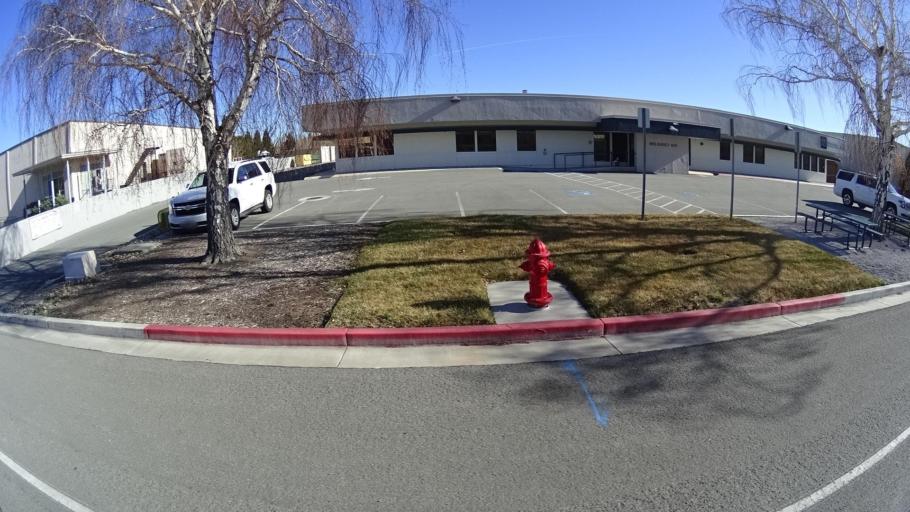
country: US
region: Nevada
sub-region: Washoe County
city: Sparks
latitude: 39.5063
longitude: -119.7609
